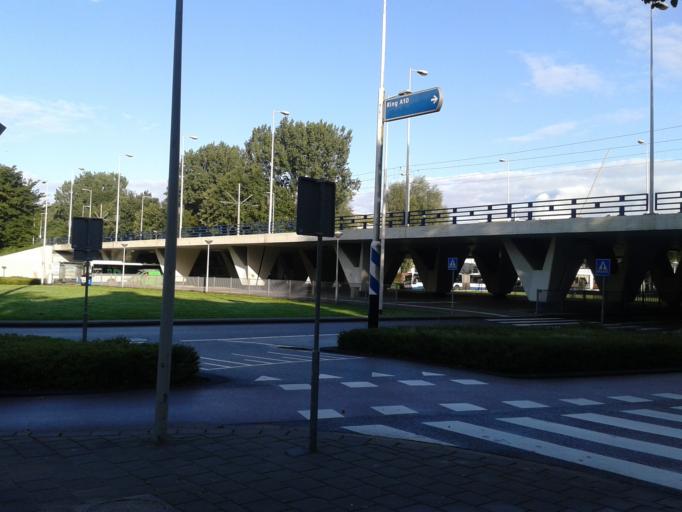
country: NL
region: North Holland
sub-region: Gemeente Amsterdam
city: Amsterdam
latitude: 52.3574
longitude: 4.8280
